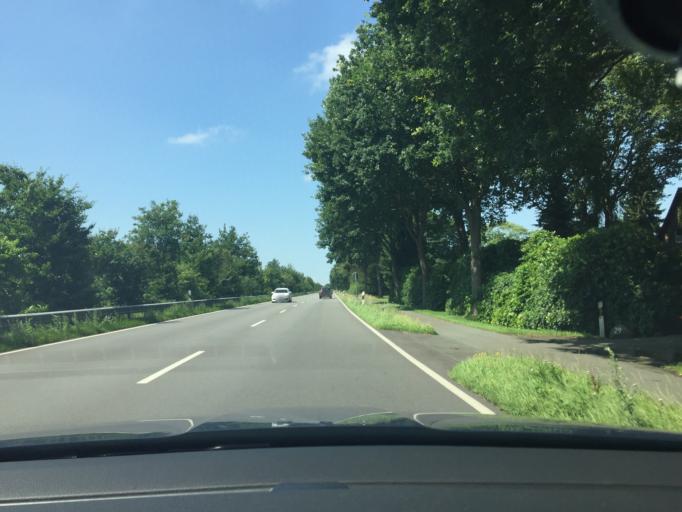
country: DE
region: Lower Saxony
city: Edewecht
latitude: 53.0843
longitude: 7.9875
